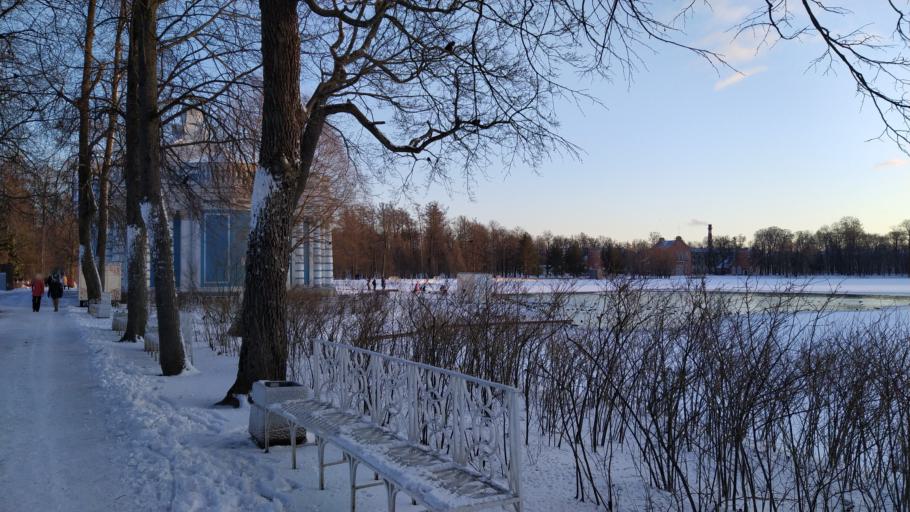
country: RU
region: St.-Petersburg
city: Pushkin
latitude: 59.7138
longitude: 30.3977
